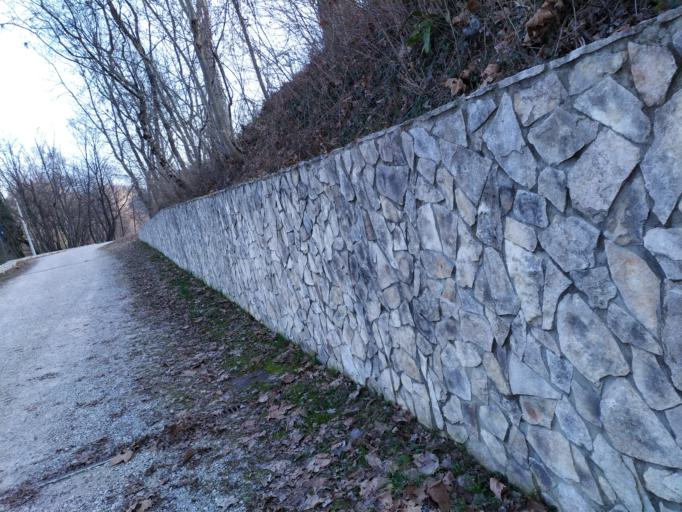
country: IT
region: Veneto
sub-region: Provincia di Vicenza
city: Cogollo del Cengio
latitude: 45.7737
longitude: 11.4118
